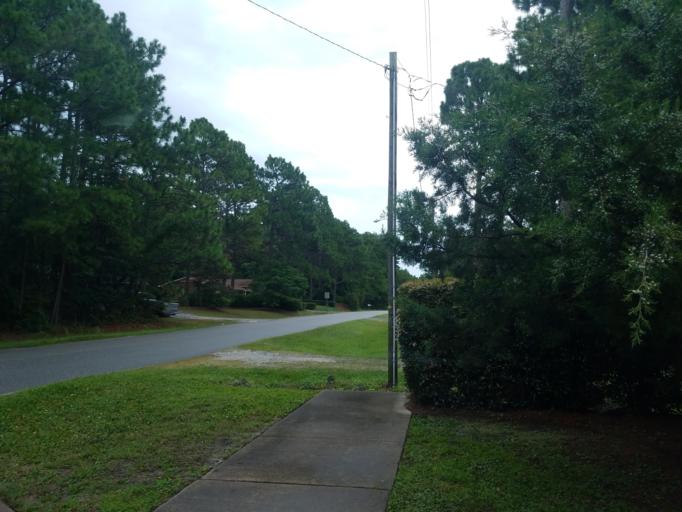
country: US
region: North Carolina
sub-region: New Hanover County
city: Kings Grant
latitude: 34.2403
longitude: -77.8638
